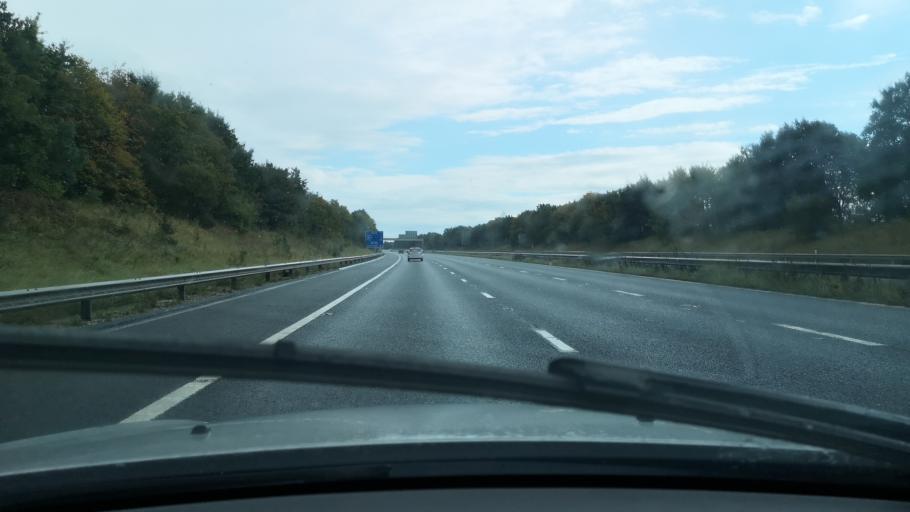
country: GB
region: England
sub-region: City and Borough of Wakefield
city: Knottingley
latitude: 53.6931
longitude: -1.2514
